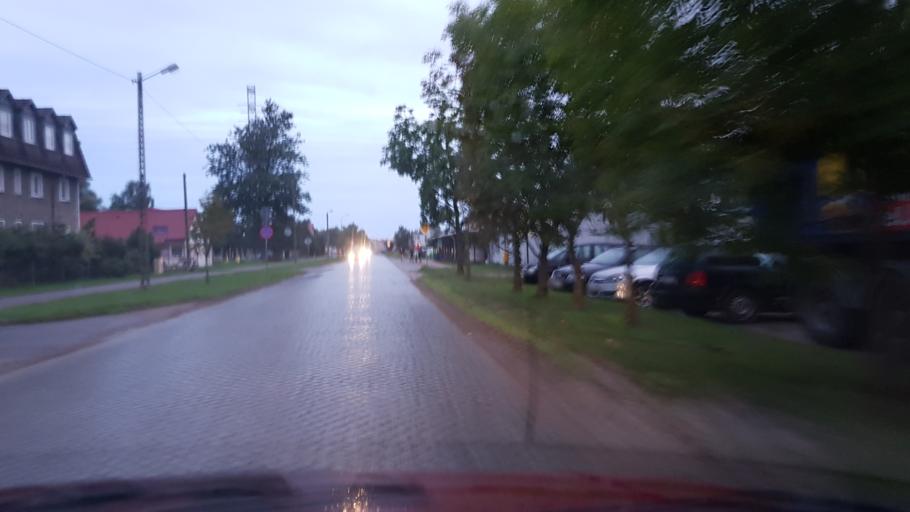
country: PL
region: West Pomeranian Voivodeship
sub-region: Powiat slawienski
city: Slawno
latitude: 54.3506
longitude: 16.6804
